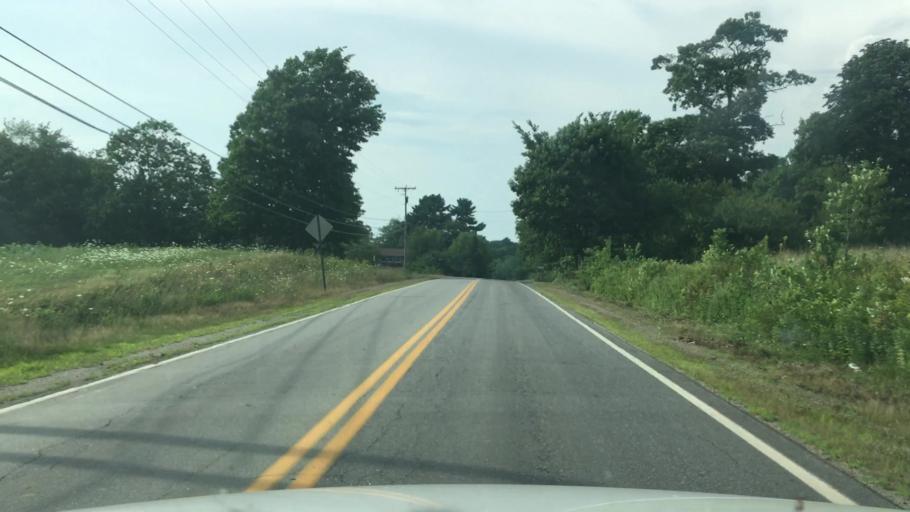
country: US
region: Maine
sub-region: Lincoln County
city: Waldoboro
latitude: 44.1243
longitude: -69.3669
